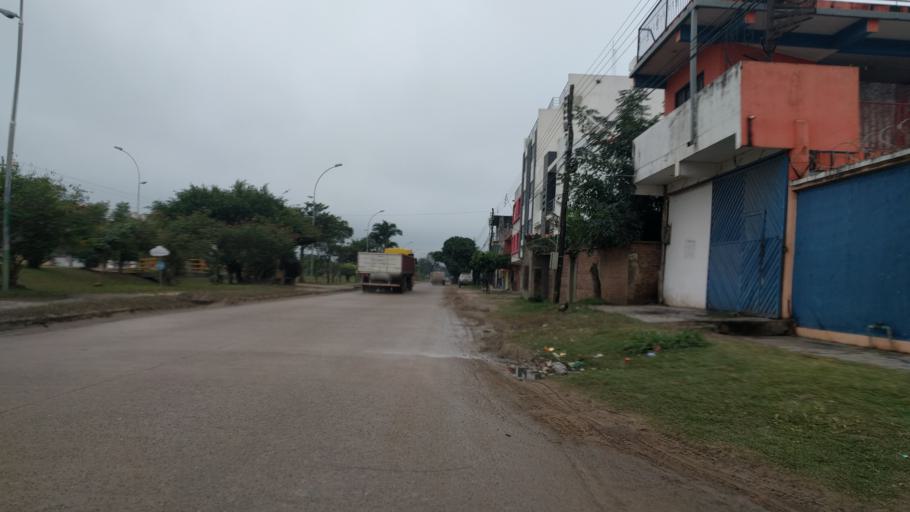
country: BO
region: Santa Cruz
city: Santa Cruz de la Sierra
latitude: -17.8192
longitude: -63.2107
